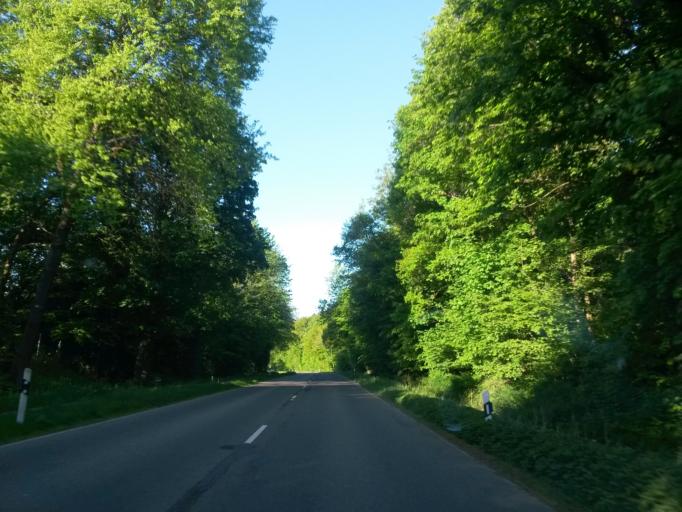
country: DE
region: North Rhine-Westphalia
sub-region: Regierungsbezirk Koln
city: Numbrecht
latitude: 50.9168
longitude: 7.4925
